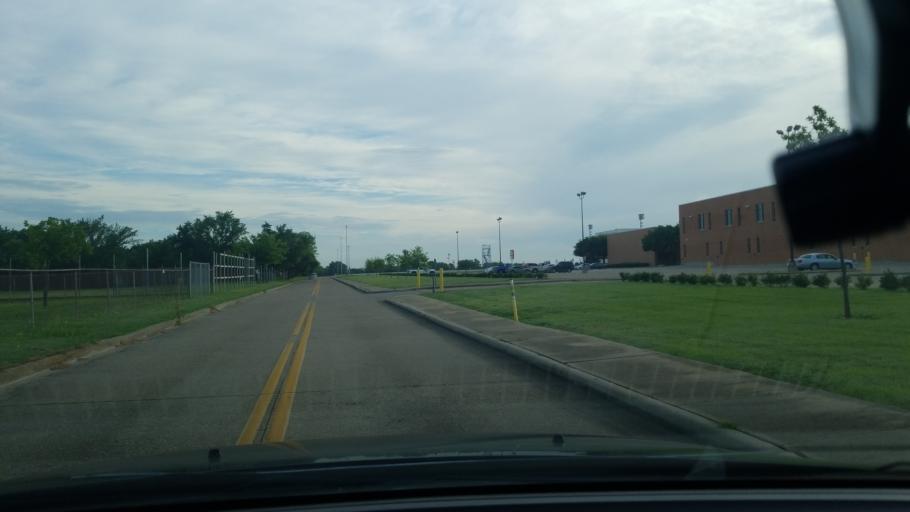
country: US
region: Texas
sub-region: Dallas County
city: Balch Springs
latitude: 32.7604
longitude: -96.6372
